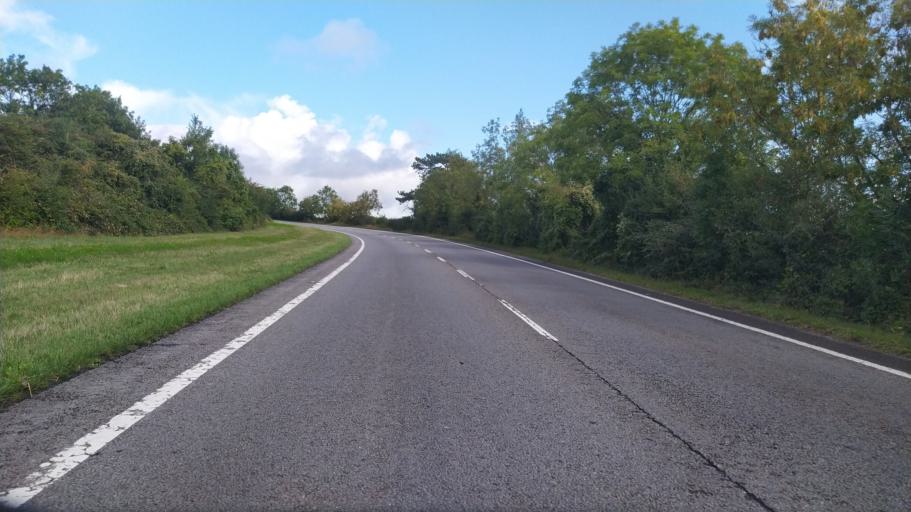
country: GB
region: England
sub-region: Dorset
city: Blandford Forum
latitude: 50.8660
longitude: -2.1465
